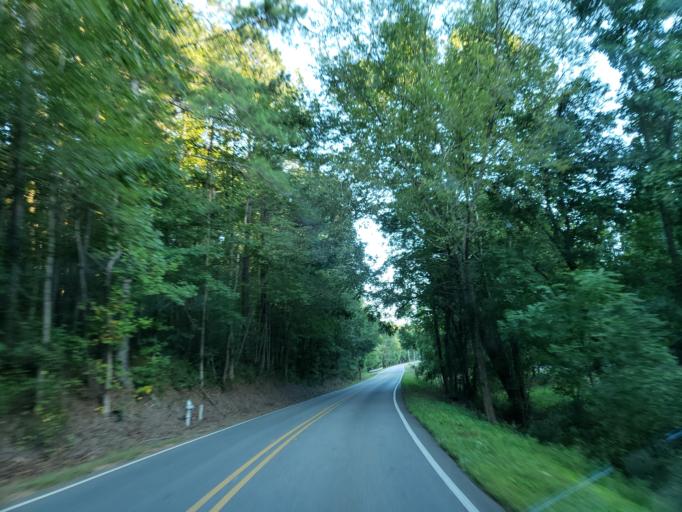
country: US
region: Georgia
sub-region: Bartow County
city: Rydal
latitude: 34.3873
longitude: -84.5922
